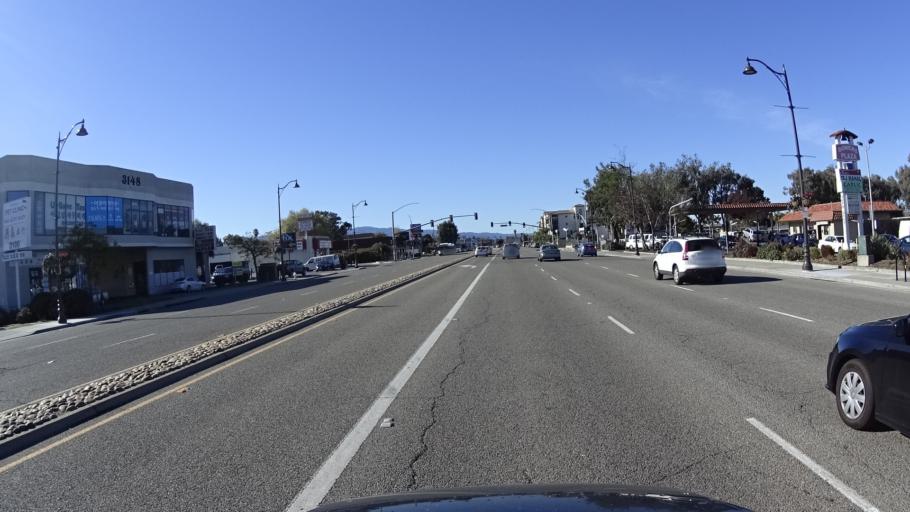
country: US
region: California
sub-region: Santa Clara County
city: Santa Clara
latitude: 37.3524
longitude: -121.9825
